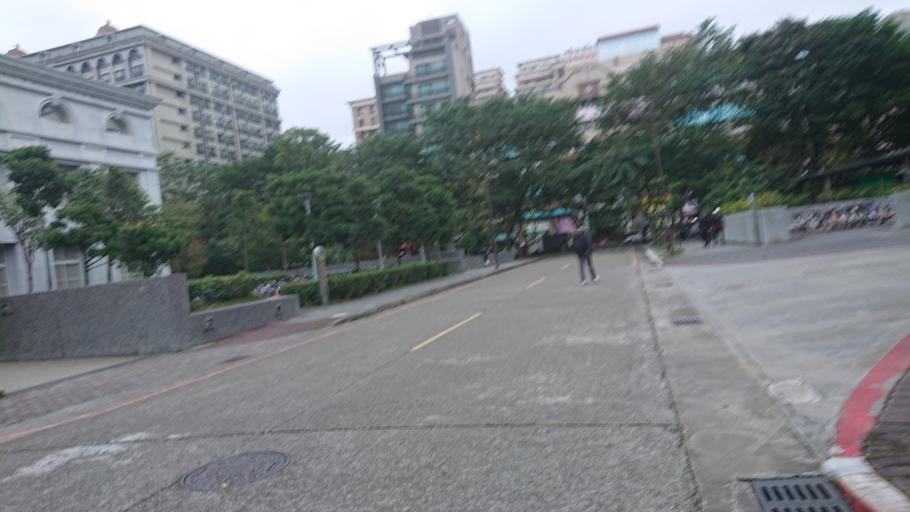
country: TW
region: Taiwan
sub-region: Taoyuan
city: Taoyuan
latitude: 24.9439
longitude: 121.3721
